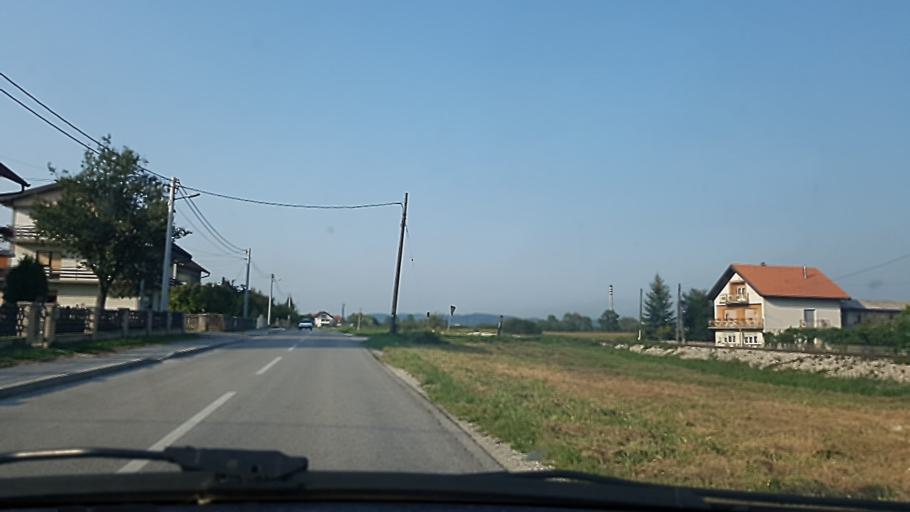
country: HR
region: Zagrebacka
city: Jakovlje
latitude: 45.9881
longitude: 15.8422
